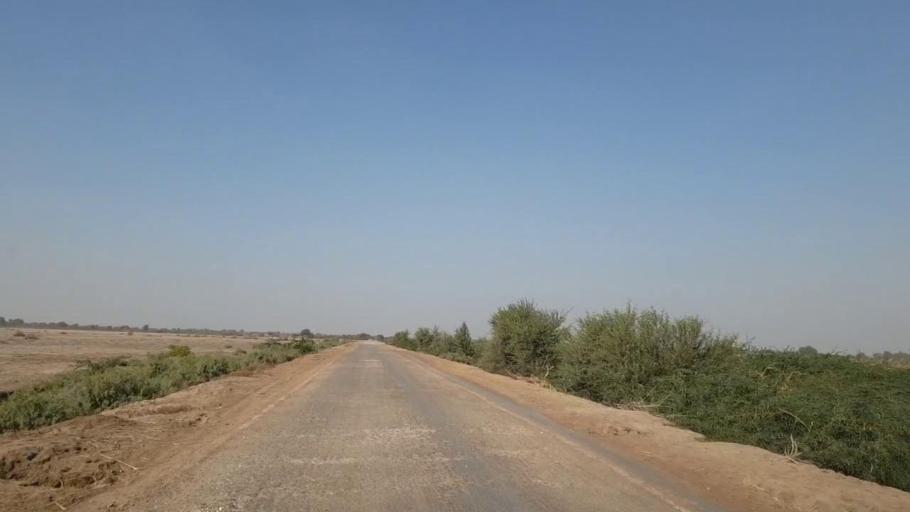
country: PK
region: Sindh
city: Digri
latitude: 24.9798
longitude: 69.1111
